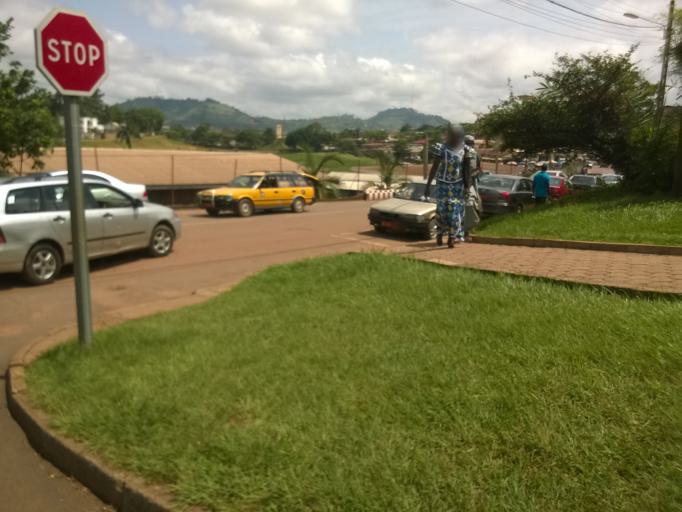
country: CM
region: Centre
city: Yaounde
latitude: 3.8657
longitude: 11.5120
